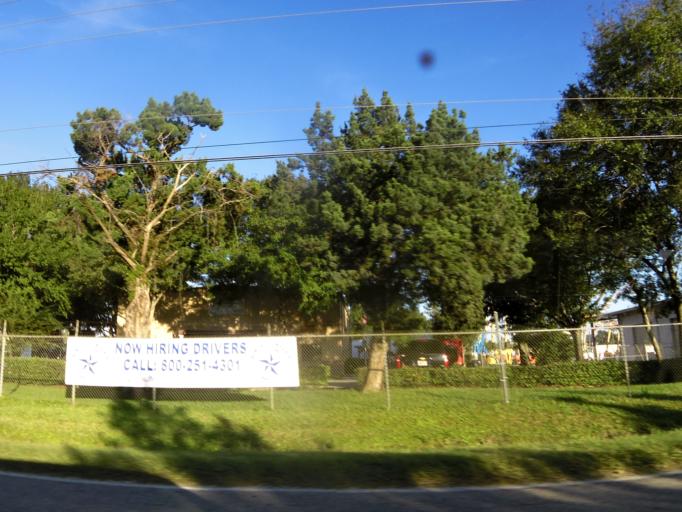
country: US
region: Florida
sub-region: Duval County
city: Jacksonville
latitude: 30.3416
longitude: -81.7646
